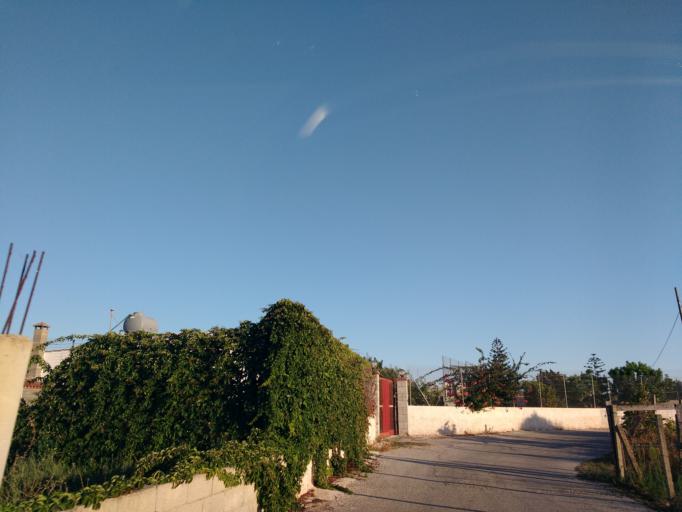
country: IT
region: Sicily
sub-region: Ragusa
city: Ispica
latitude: 36.7218
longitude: 14.9201
